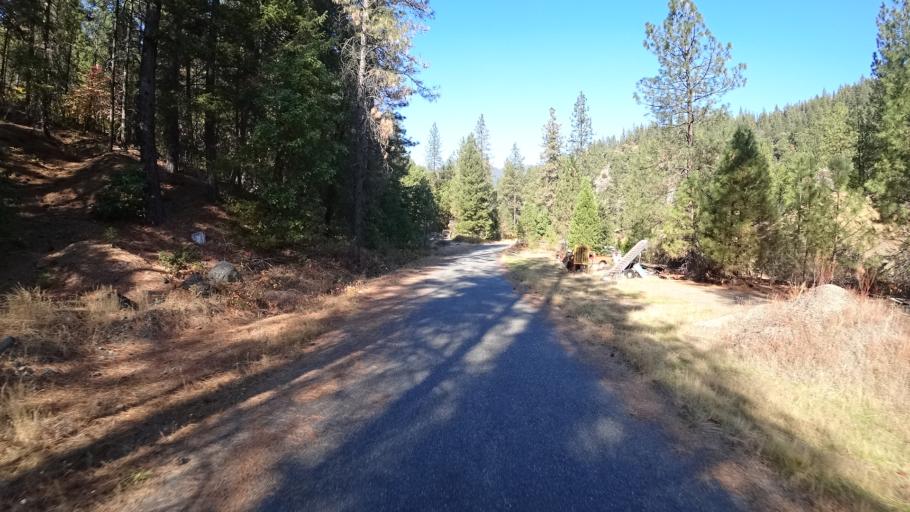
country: US
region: California
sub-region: Siskiyou County
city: Happy Camp
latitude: 41.7726
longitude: -123.0297
